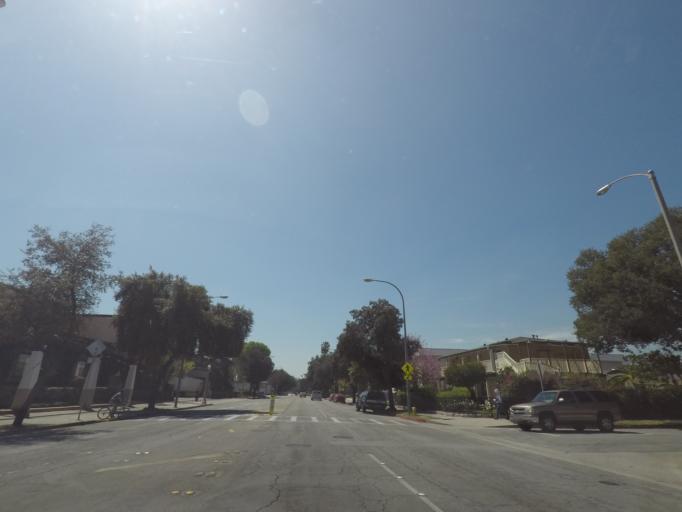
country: US
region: California
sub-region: Los Angeles County
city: Pasadena
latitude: 34.1573
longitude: -118.1520
